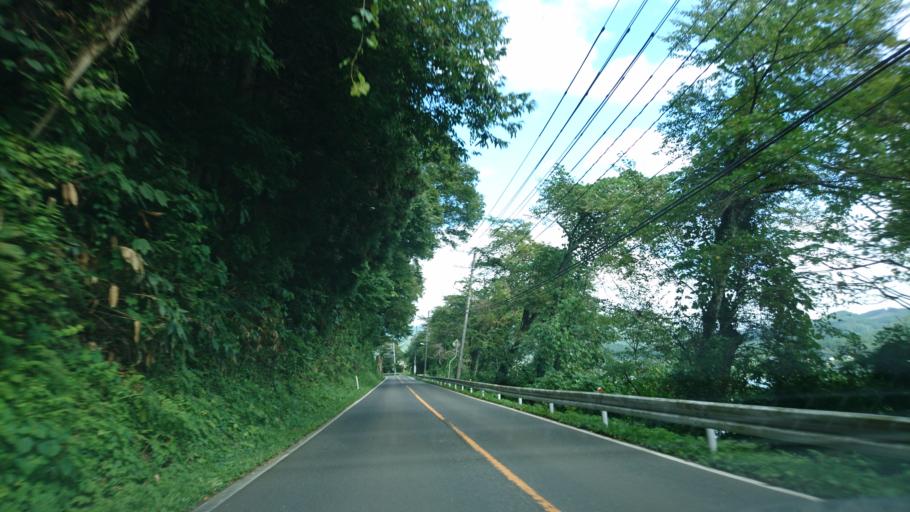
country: JP
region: Miyagi
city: Furukawa
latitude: 38.7822
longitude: 140.8506
